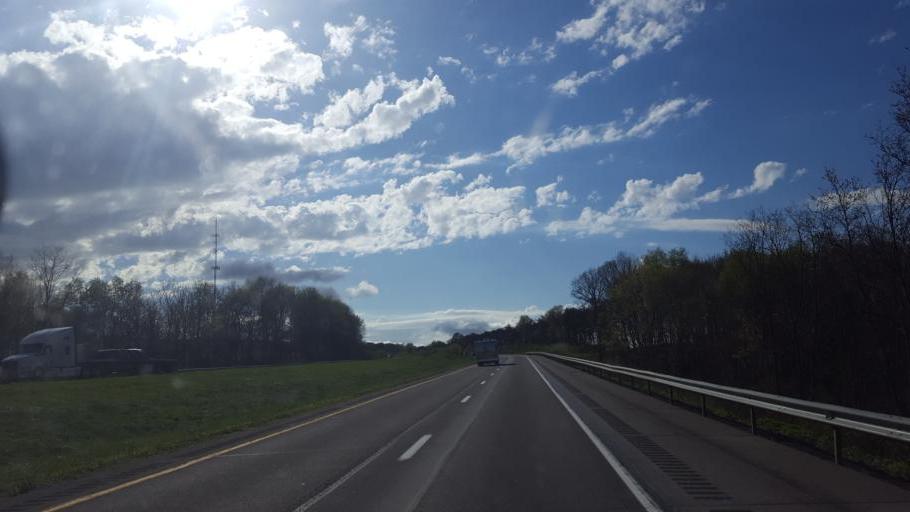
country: US
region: Pennsylvania
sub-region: Venango County
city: Franklin
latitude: 41.1956
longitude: -79.8125
